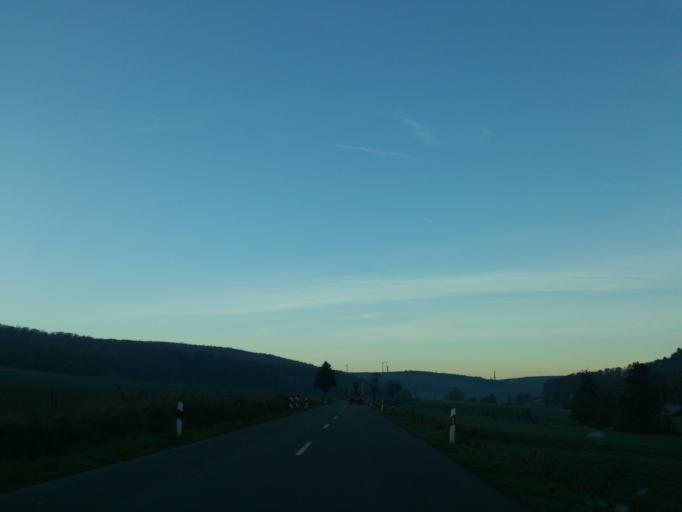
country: DE
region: North Rhine-Westphalia
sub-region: Regierungsbezirk Detmold
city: Altenbeken
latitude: 51.7060
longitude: 8.9011
